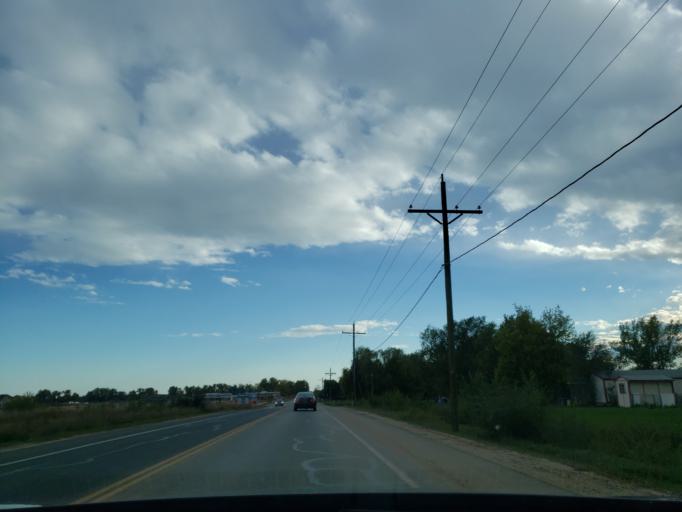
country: US
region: Colorado
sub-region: Larimer County
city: Fort Collins
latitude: 40.5947
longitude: -105.0294
